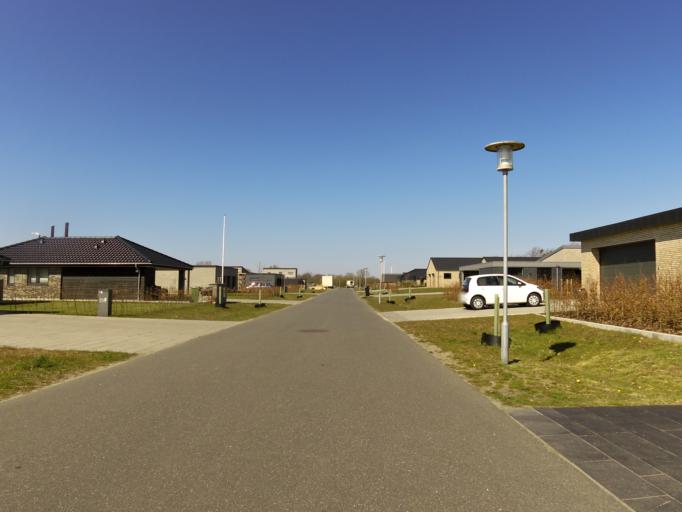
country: DK
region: South Denmark
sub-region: Esbjerg Kommune
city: Ribe
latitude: 55.3390
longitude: 8.7950
